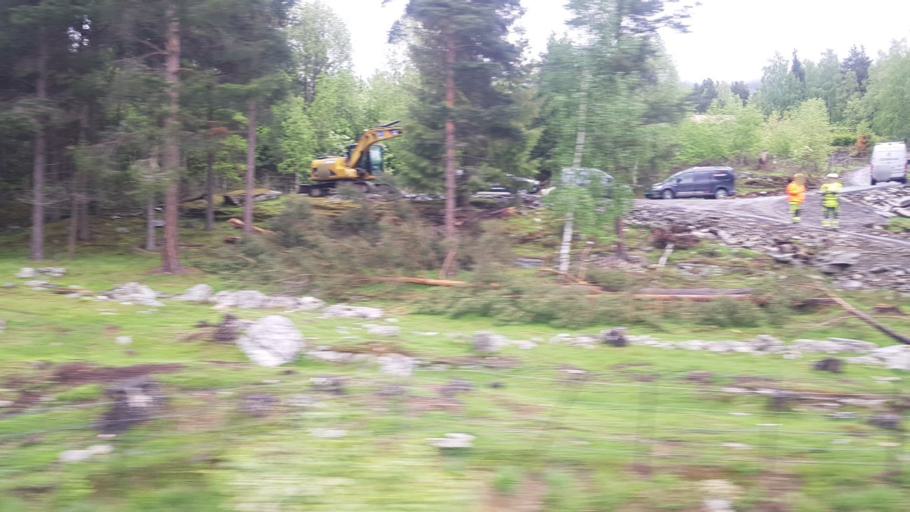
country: NO
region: Oppland
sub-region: Sor-Fron
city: Hundorp
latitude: 61.5553
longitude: 9.9443
